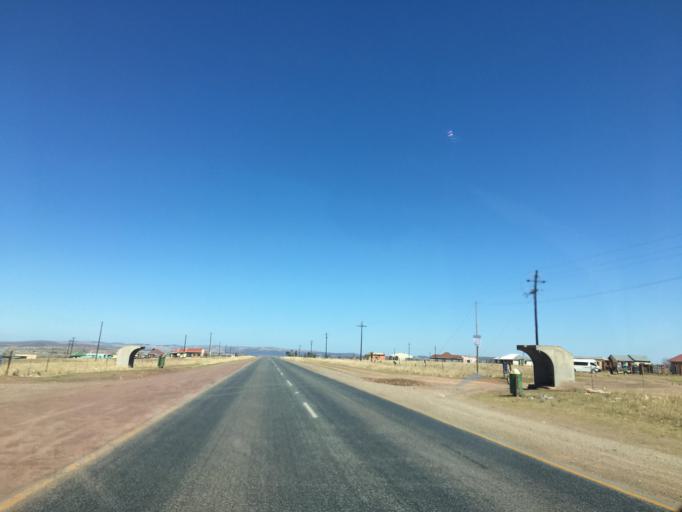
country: ZA
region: Eastern Cape
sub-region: Chris Hani District Municipality
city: Cofimvaba
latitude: -31.9284
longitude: 27.8376
